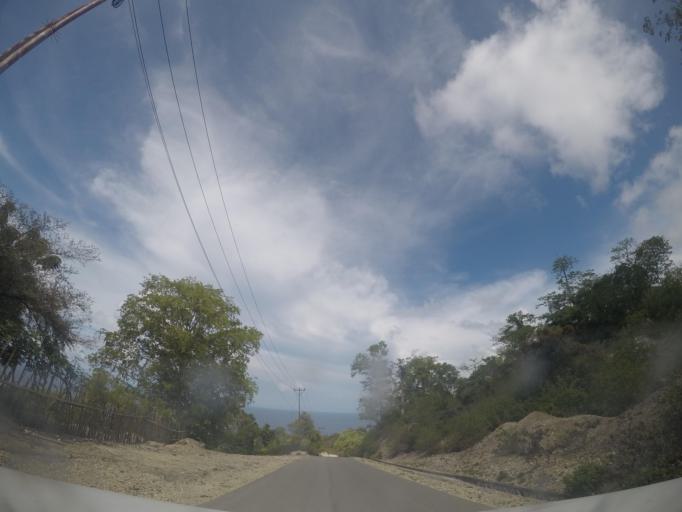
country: TL
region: Lautem
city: Lospalos
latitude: -8.3649
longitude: 127.0526
